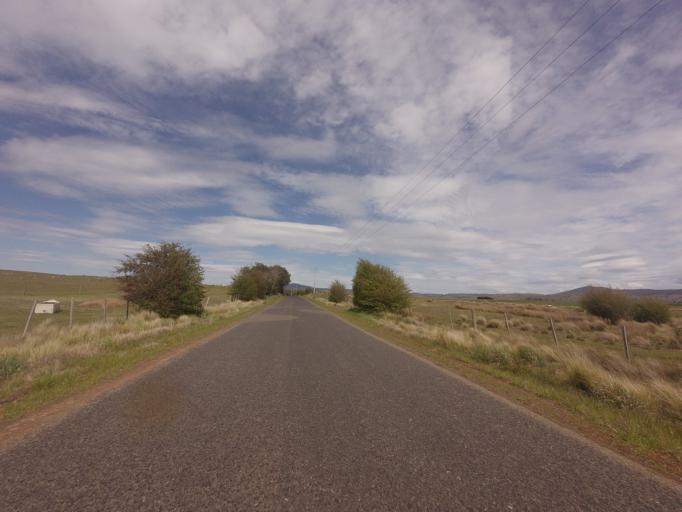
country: AU
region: Tasmania
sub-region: Northern Midlands
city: Evandale
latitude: -41.8717
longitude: 147.3530
